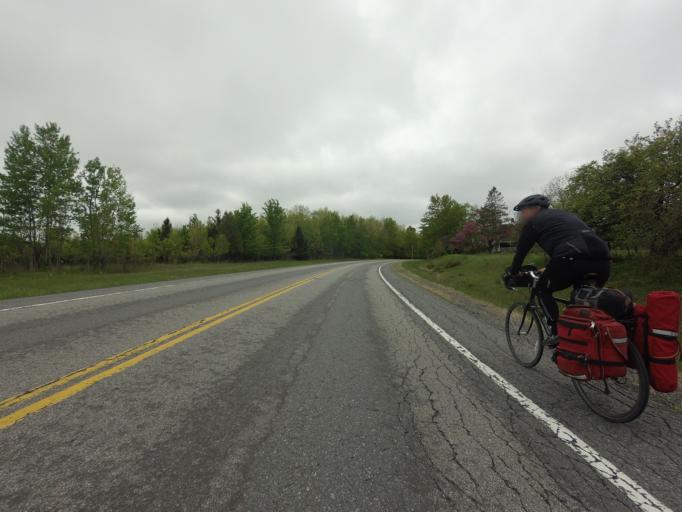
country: US
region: New York
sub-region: St. Lawrence County
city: Norfolk
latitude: 44.9924
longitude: -75.1588
